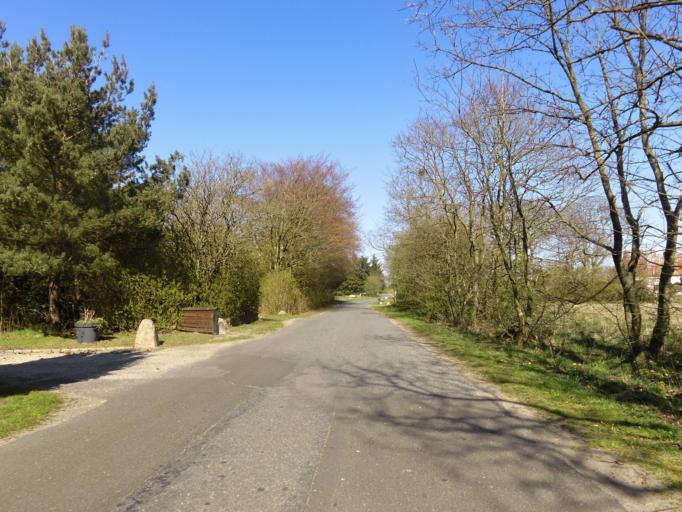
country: DK
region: South Denmark
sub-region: Esbjerg Kommune
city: Ribe
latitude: 55.3551
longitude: 8.7938
